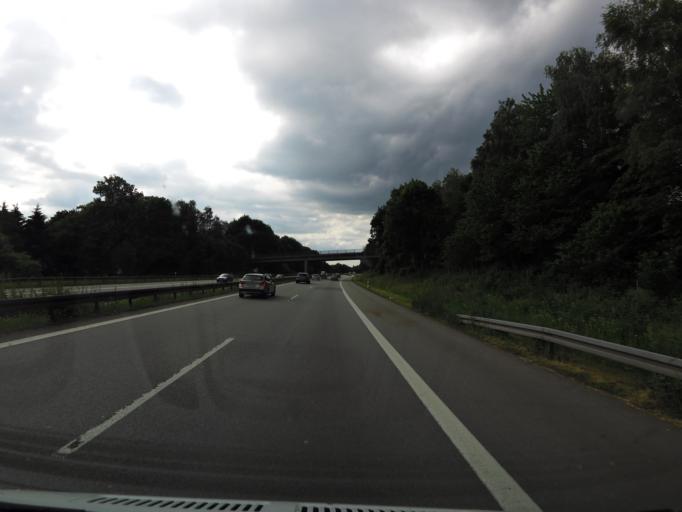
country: DE
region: Bavaria
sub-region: Lower Bavaria
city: Aussernzell
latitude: 48.7058
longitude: 13.1738
